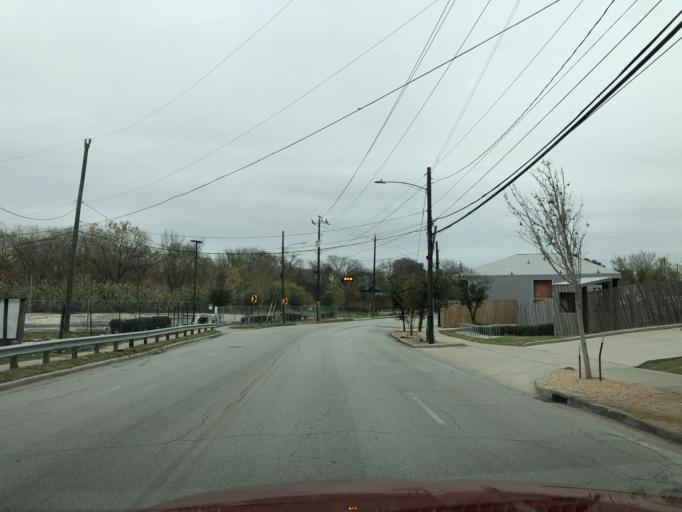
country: US
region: Texas
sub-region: Harris County
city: Houston
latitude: 29.7859
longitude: -95.3667
